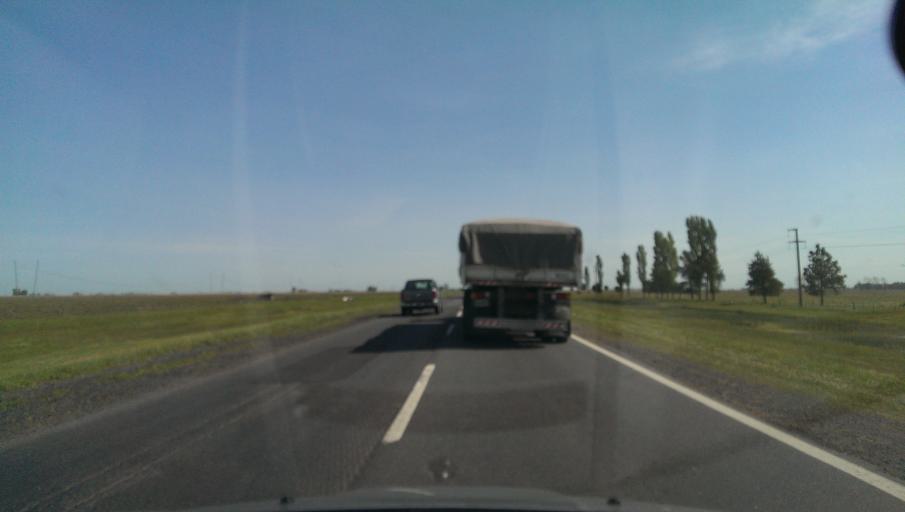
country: AR
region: Buenos Aires
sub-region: Partido de Azul
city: Azul
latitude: -36.6144
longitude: -59.6818
